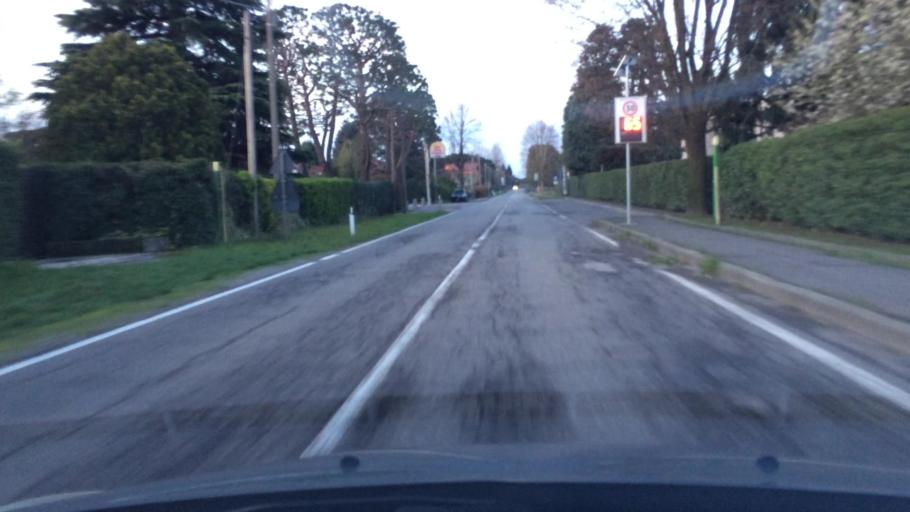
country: IT
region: Lombardy
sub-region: Provincia di Como
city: Puginate
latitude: 45.7062
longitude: 9.0630
